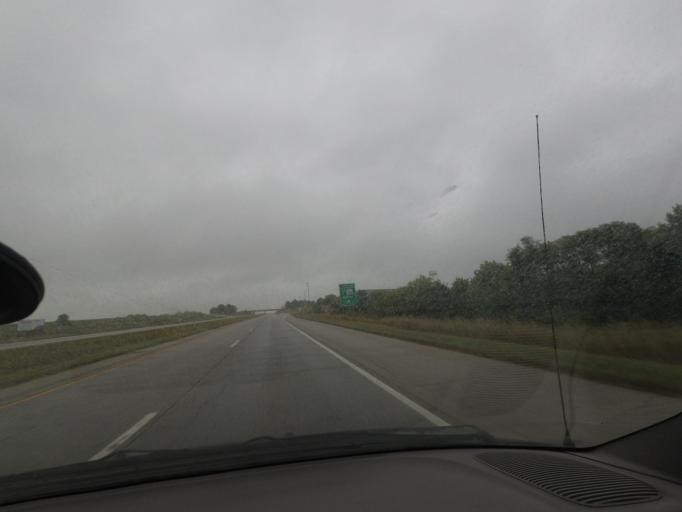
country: US
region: Illinois
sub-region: Pike County
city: Barry
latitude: 39.7064
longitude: -91.0465
